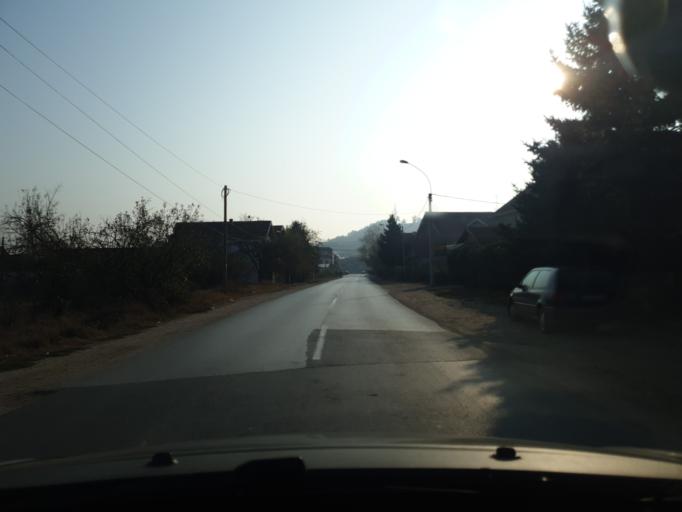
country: RS
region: Central Serbia
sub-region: Jablanicki Okrug
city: Leskovac
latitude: 42.9959
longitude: 21.9279
